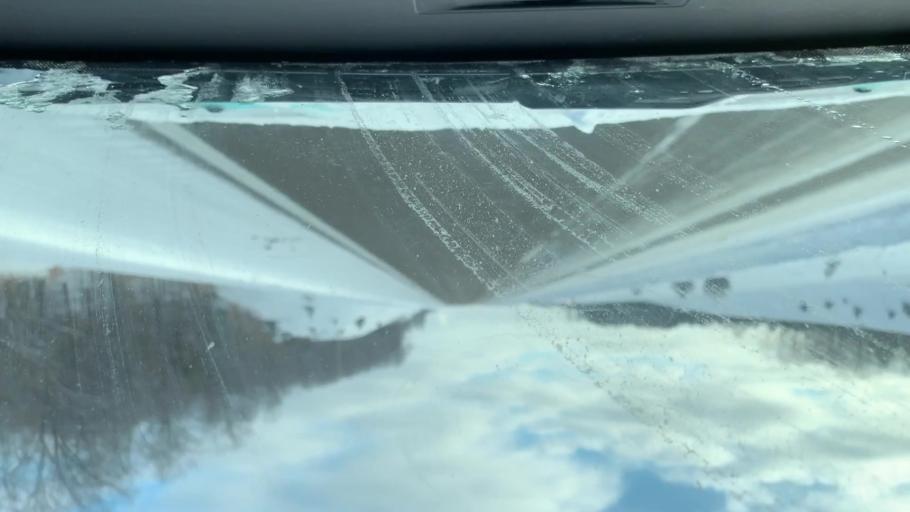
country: US
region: Michigan
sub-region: Wexford County
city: Manton
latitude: 44.3530
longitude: -85.4041
